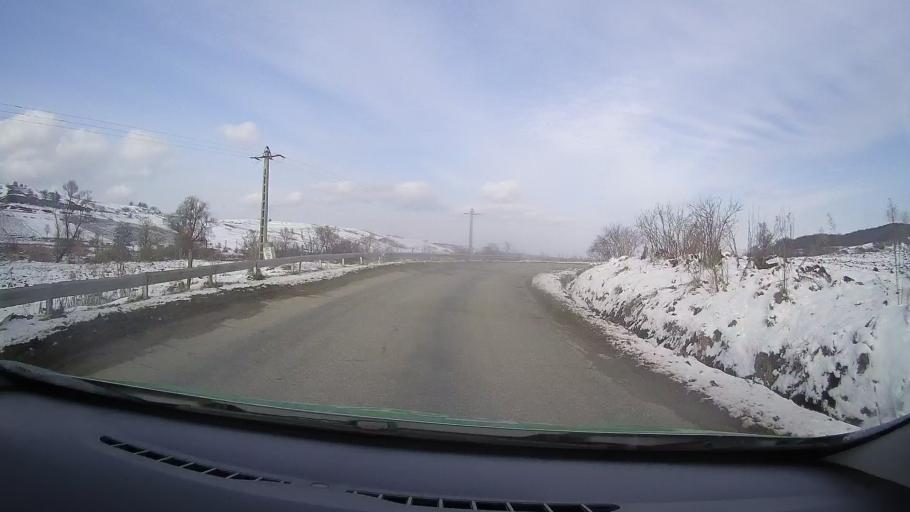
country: RO
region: Sibiu
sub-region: Oras Agnita
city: Ruja
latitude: 45.9858
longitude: 24.6585
